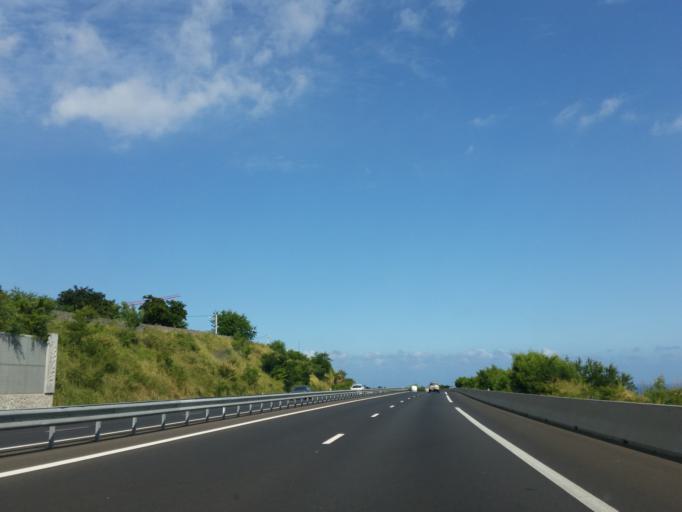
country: RE
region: Reunion
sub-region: Reunion
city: Saint-Leu
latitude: -21.1894
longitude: 55.2968
